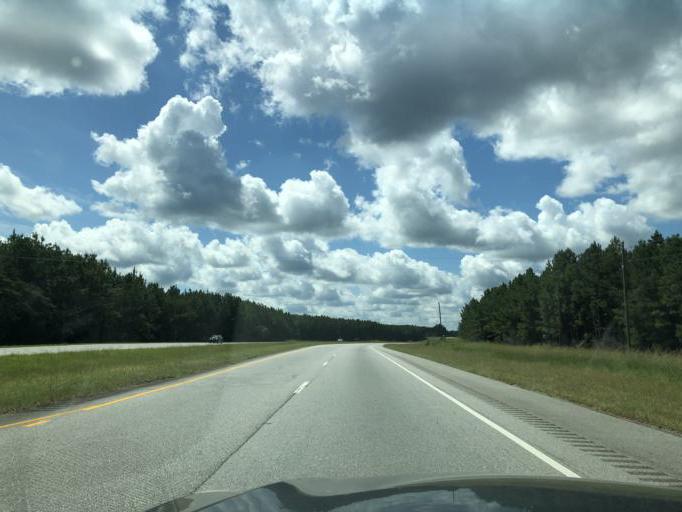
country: US
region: Alabama
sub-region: Russell County
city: Ladonia
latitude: 32.2195
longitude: -85.1693
